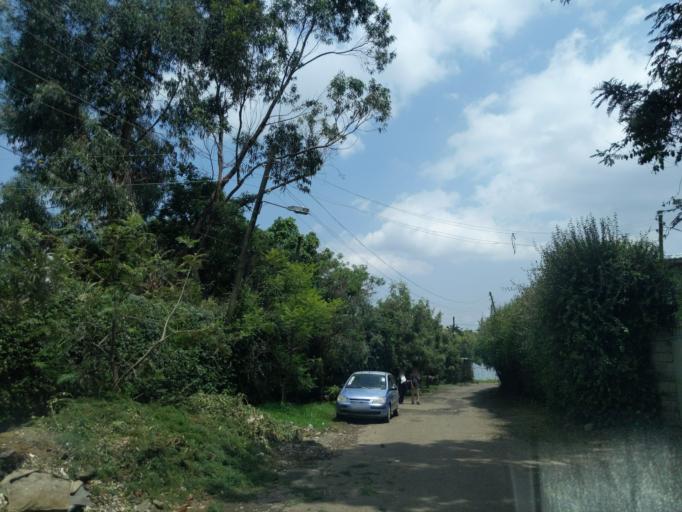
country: ET
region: Adis Abeba
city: Addis Ababa
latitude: 9.0182
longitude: 38.7796
